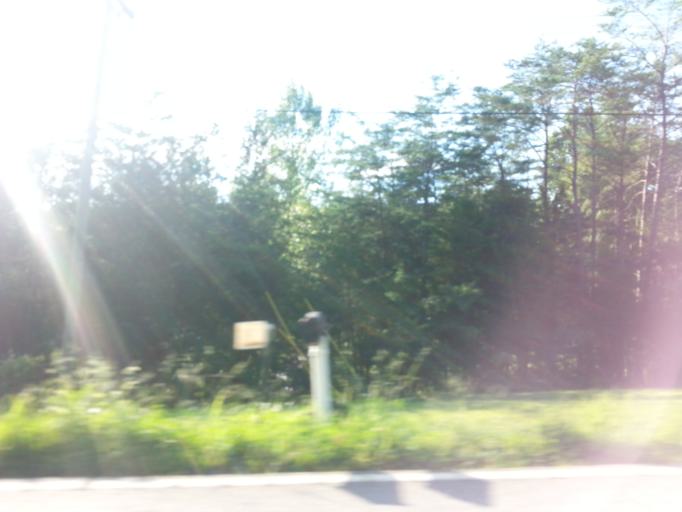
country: US
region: Tennessee
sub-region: Blount County
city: Maryville
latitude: 35.6397
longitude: -83.9973
